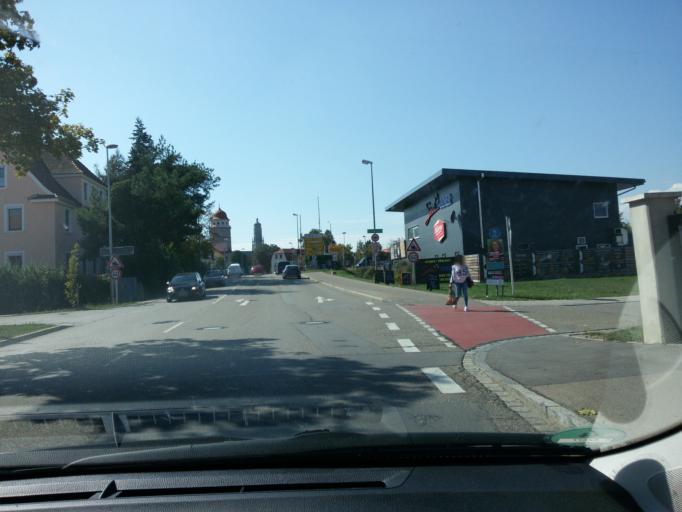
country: DE
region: Bavaria
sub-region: Swabia
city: Noerdlingen
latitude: 48.8565
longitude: 10.4949
